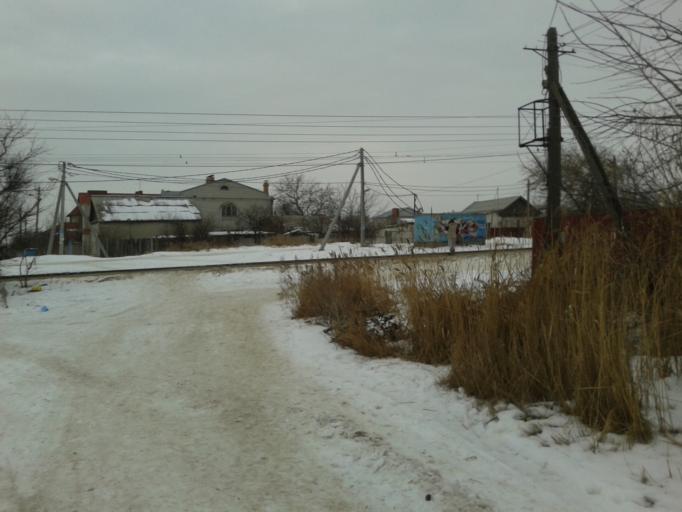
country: RU
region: Volgograd
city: Volgograd
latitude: 48.7275
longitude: 44.5053
